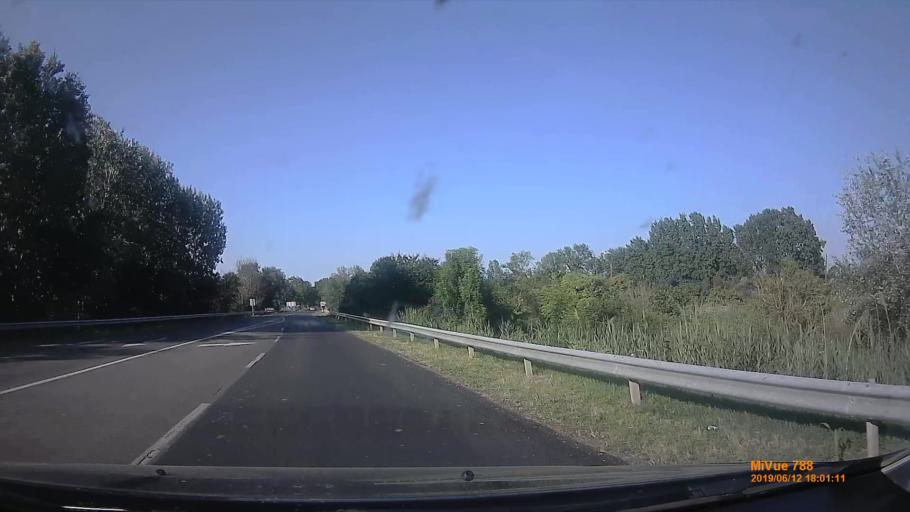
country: HU
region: Csongrad
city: Roszke
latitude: 46.2244
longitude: 20.0714
